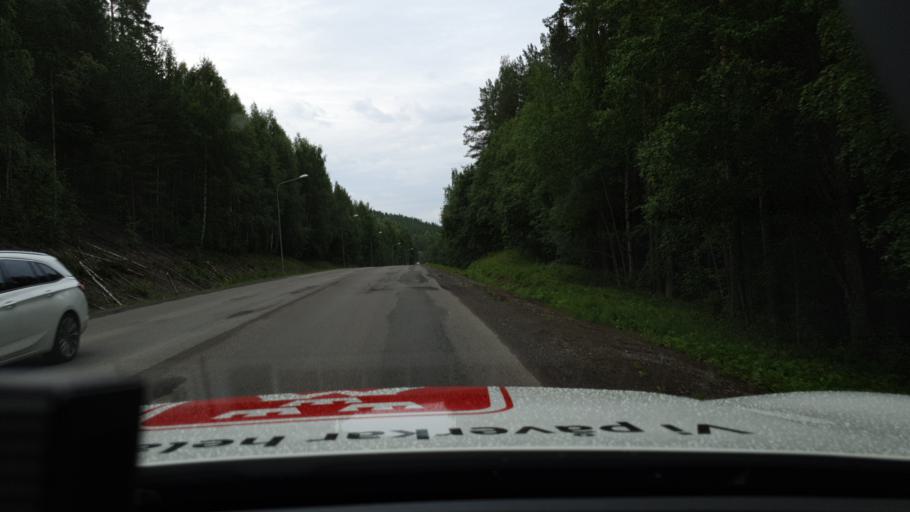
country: SE
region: Norrbotten
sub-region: Bodens Kommun
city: Boden
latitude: 65.8419
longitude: 21.6048
